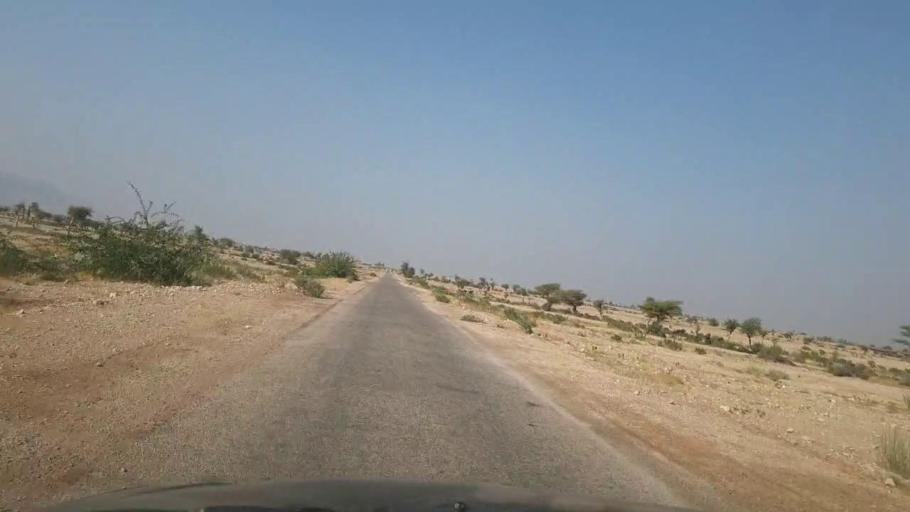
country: PK
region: Sindh
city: Jamshoro
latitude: 25.5951
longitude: 67.8175
